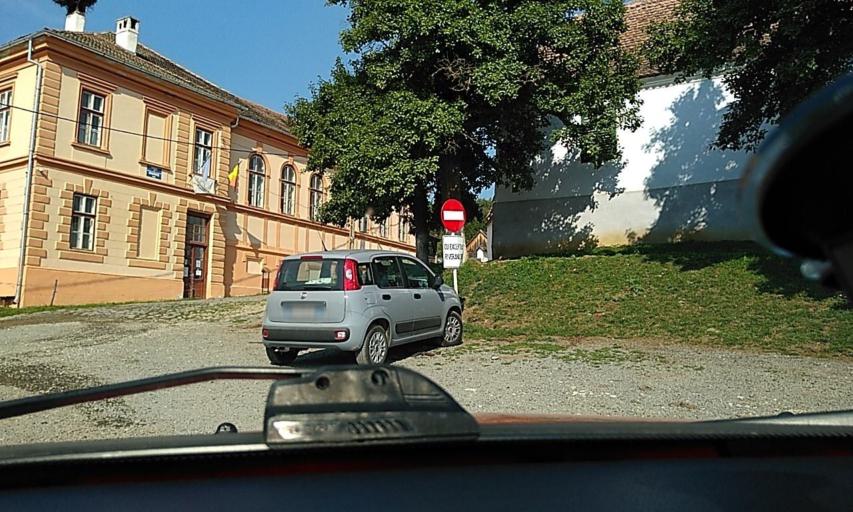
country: RO
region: Brasov
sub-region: Comuna Jibert
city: Jibert
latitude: 46.0538
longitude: 25.0919
